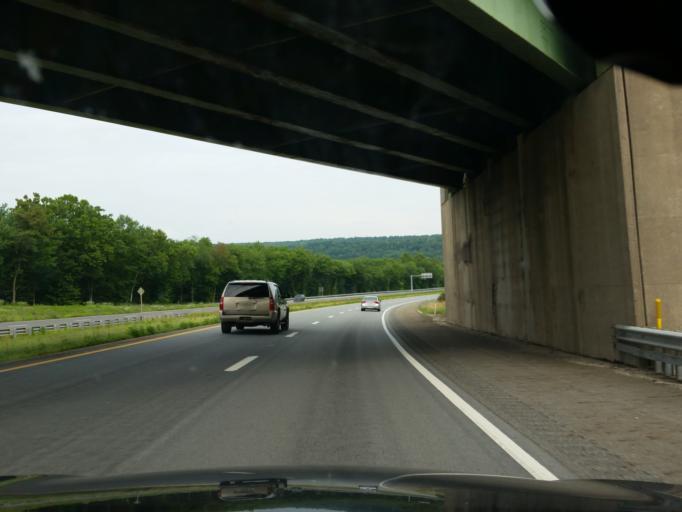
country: US
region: Pennsylvania
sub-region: Perry County
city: Newport
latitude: 40.5433
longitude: -77.1502
